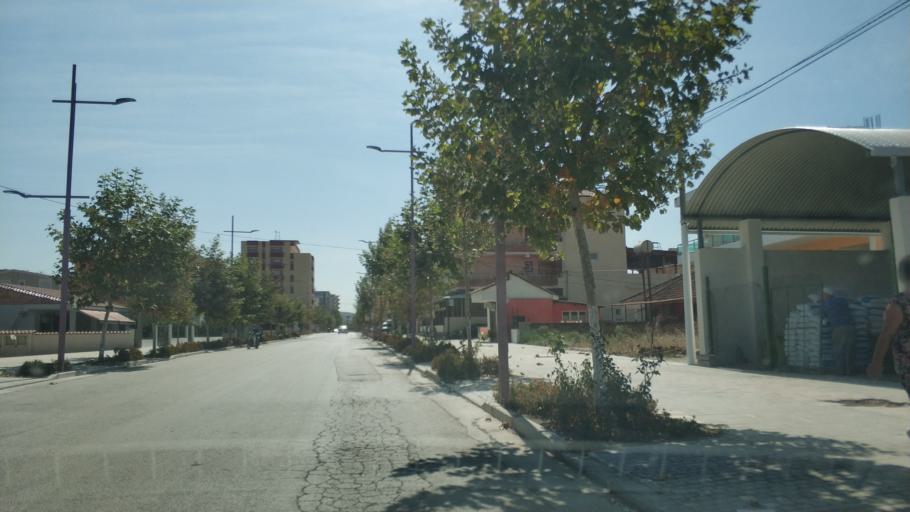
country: AL
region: Fier
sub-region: Rrethi i Lushnjes
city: Divjake
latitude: 41.0006
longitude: 19.5309
